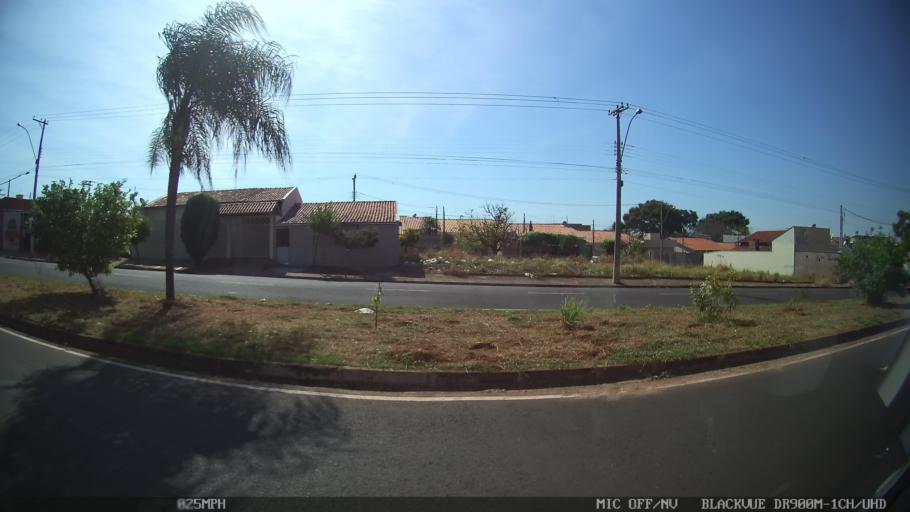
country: BR
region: Sao Paulo
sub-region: Sao Jose Do Rio Preto
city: Sao Jose do Rio Preto
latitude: -20.7907
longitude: -49.4363
